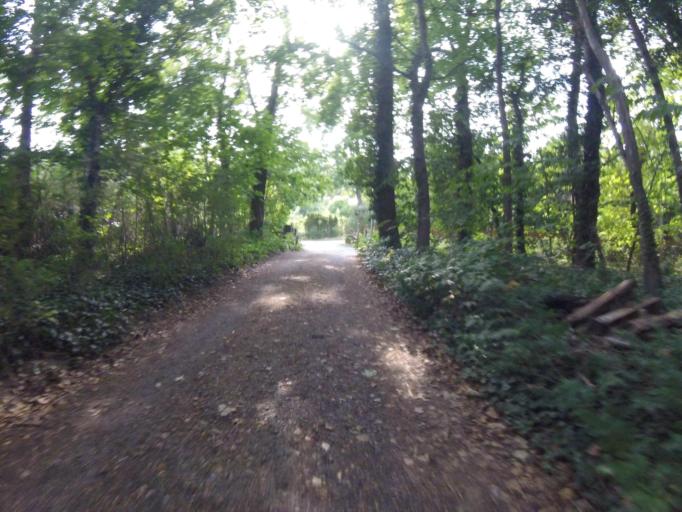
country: DE
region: Brandenburg
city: Munchehofe
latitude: 52.2424
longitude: 13.7762
